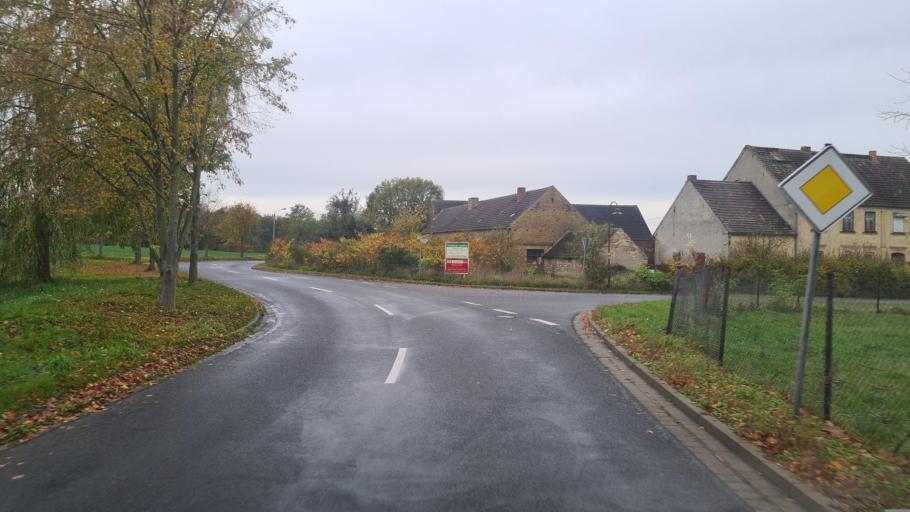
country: DE
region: Saxony-Anhalt
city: Abtsdorf
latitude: 51.9158
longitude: 12.6789
